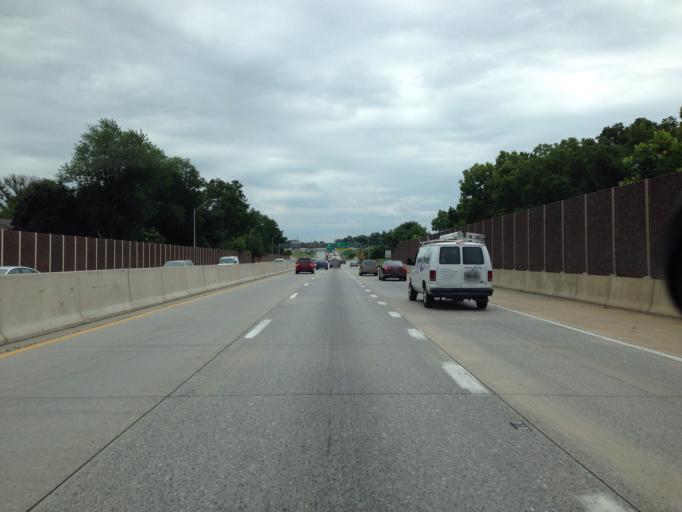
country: US
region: Pennsylvania
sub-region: Lancaster County
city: Lancaster
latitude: 40.0644
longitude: -76.2833
